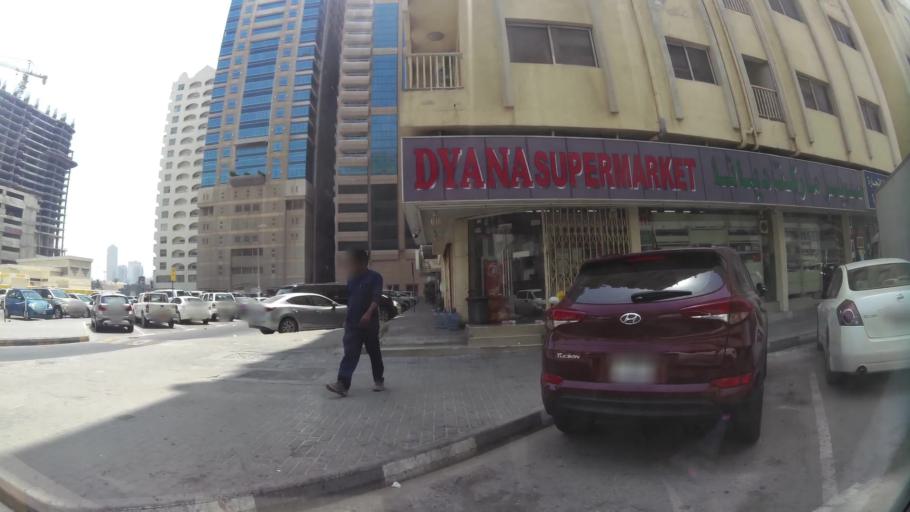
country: AE
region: Ash Shariqah
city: Sharjah
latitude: 25.3349
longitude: 55.3901
